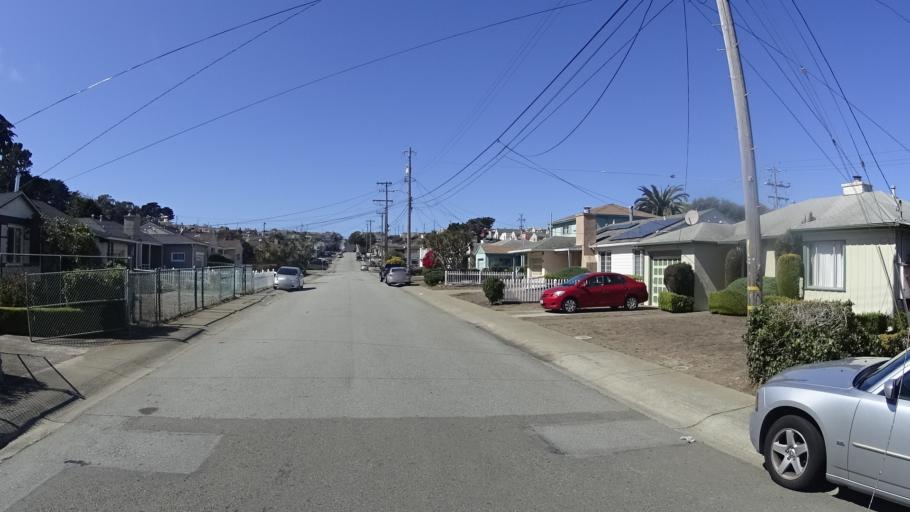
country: US
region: California
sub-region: San Mateo County
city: Broadmoor
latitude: 37.6959
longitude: -122.4854
